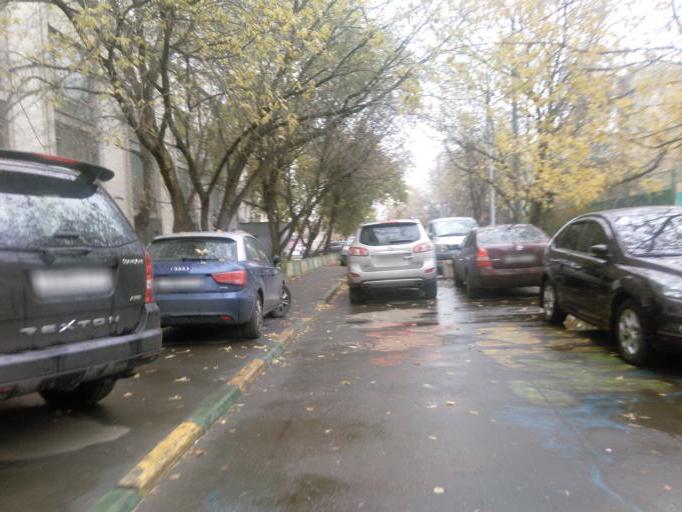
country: RU
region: Moscow
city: Zamoskvorech'ye
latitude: 55.7081
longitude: 37.6204
